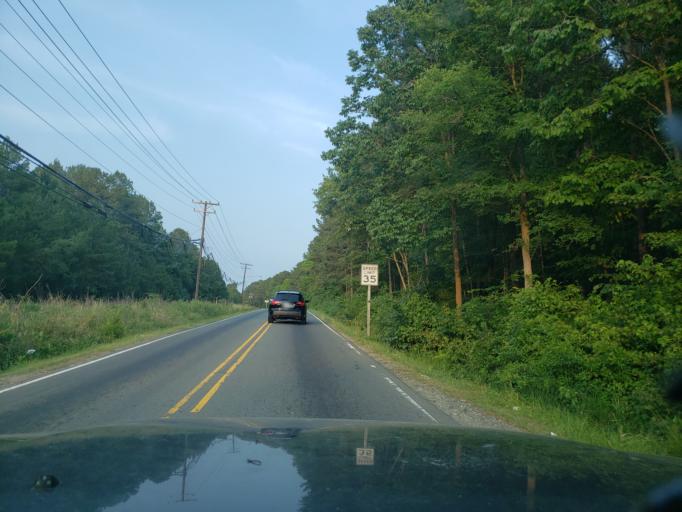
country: US
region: North Carolina
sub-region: Durham County
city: Durham
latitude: 35.9567
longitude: -78.8831
